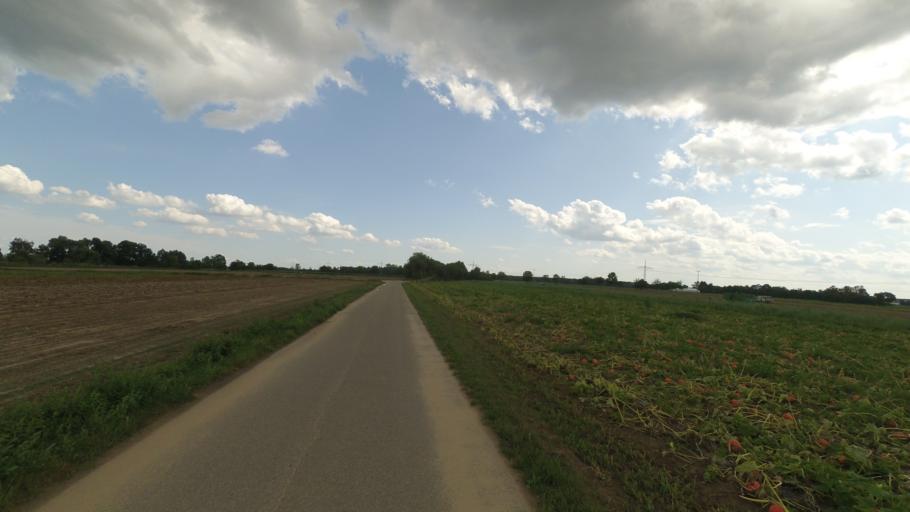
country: DE
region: Rheinland-Pfalz
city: Limburgerhof
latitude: 49.4015
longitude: 8.3991
